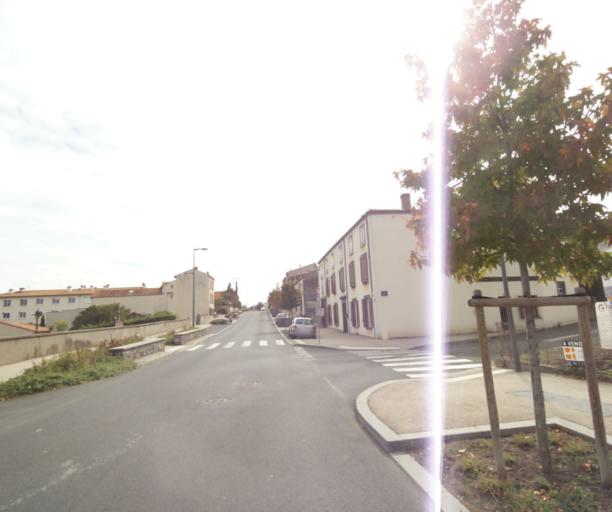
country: FR
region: Auvergne
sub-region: Departement du Puy-de-Dome
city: Perignat-les-Sarlieve
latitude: 45.7380
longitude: 3.1408
